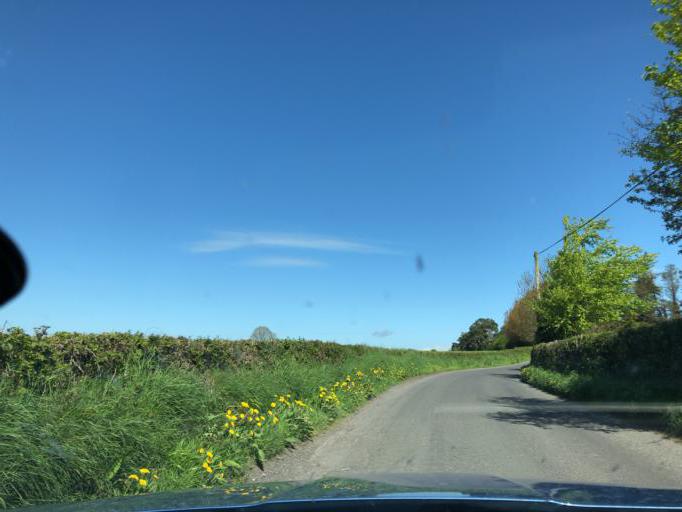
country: IE
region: Connaught
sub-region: County Galway
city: Portumna
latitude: 53.1504
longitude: -8.2927
